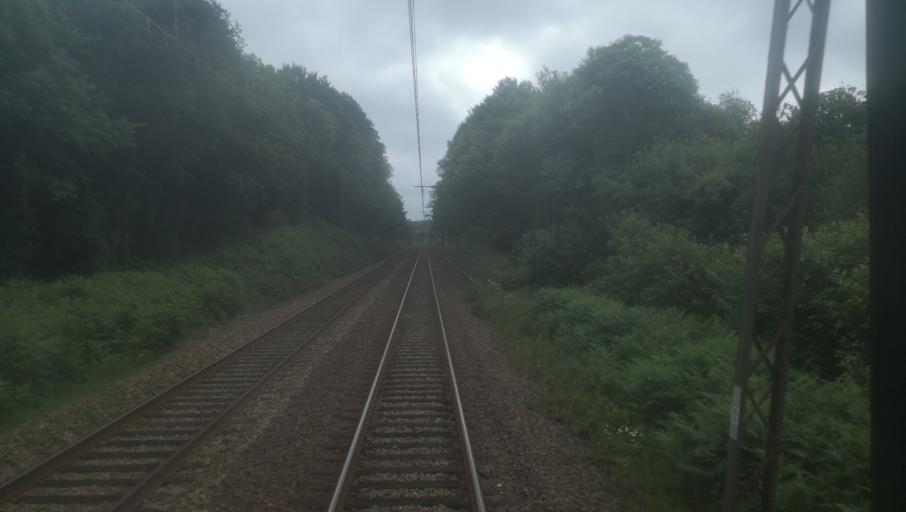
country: FR
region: Limousin
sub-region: Departement de la Haute-Vienne
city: Ambazac
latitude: 45.9633
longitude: 1.4423
